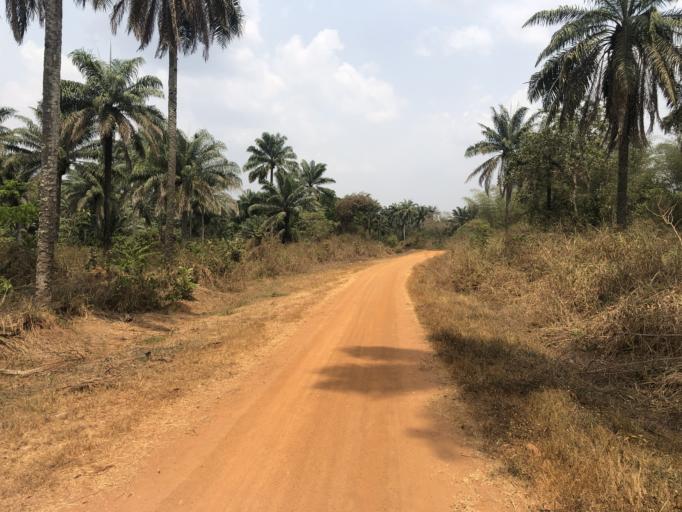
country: NG
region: Osun
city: Bode Osi
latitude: 7.7607
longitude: 4.2710
